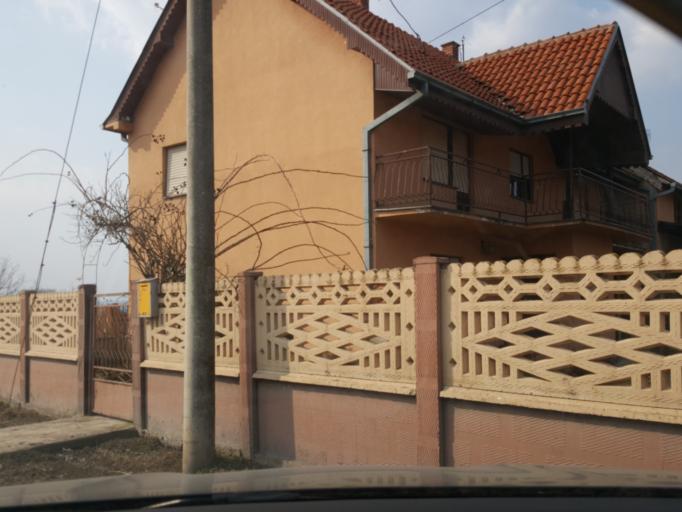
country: RS
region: Central Serbia
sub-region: Nisavski Okrug
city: Aleksinac
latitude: 43.4483
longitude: 21.7841
